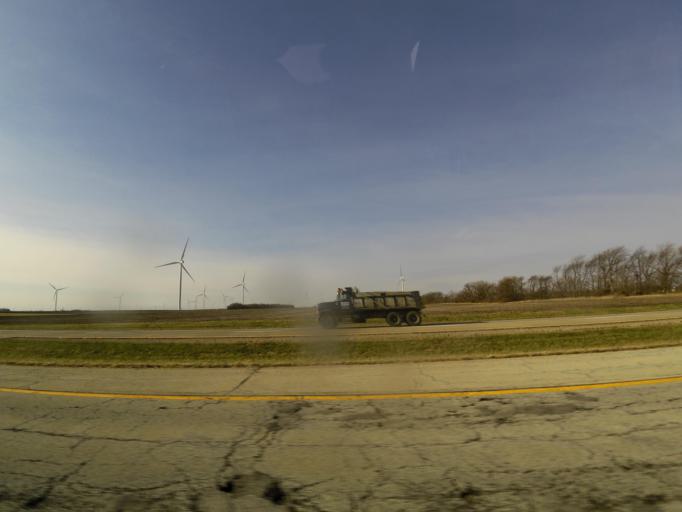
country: US
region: Illinois
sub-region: Macon County
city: Maroa
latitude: 39.9853
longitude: -88.9561
